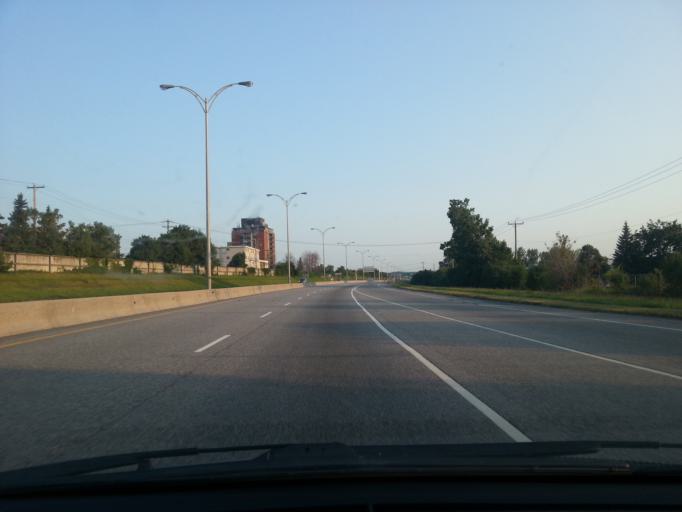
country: CA
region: Quebec
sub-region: Outaouais
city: Gatineau
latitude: 45.4507
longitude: -75.7338
